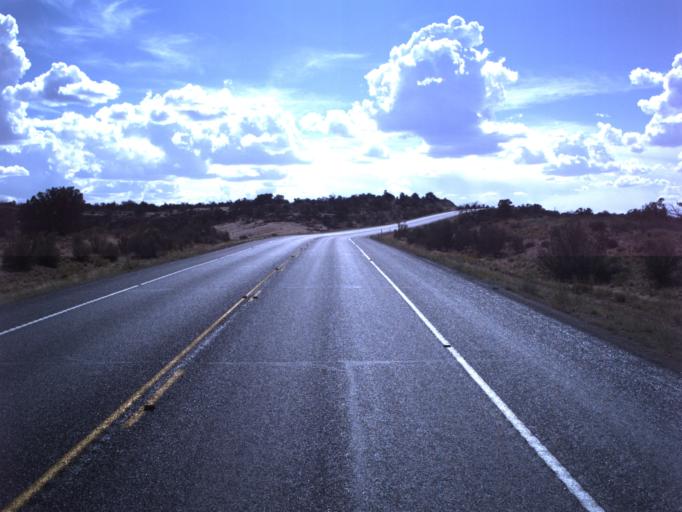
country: US
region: Utah
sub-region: Grand County
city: Moab
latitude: 38.6338
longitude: -109.7942
